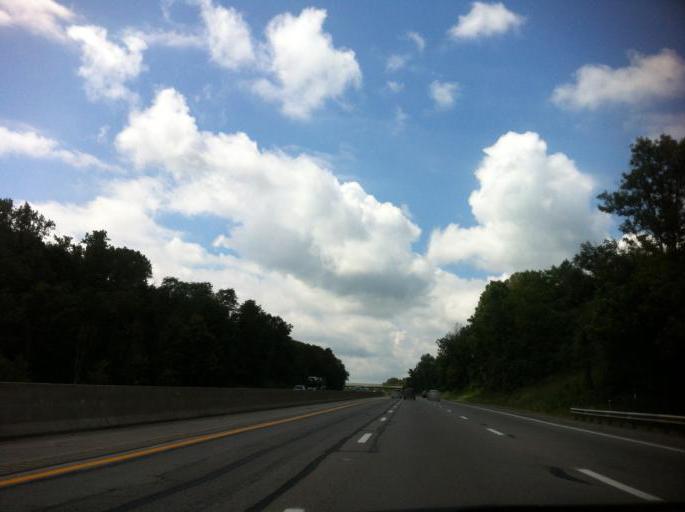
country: US
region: Ohio
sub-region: Lorain County
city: Vermilion
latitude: 41.3408
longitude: -82.3536
